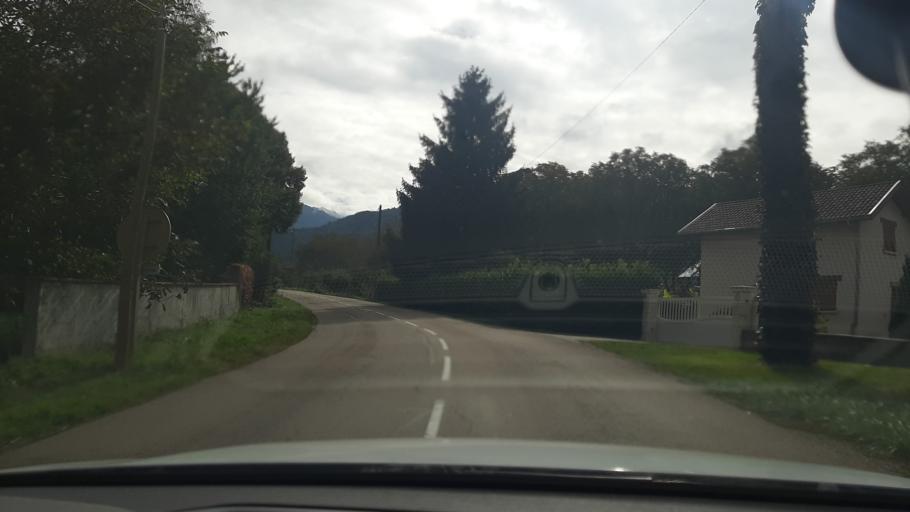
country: FR
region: Rhone-Alpes
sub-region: Departement de la Savoie
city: Montmelian
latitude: 45.4510
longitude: 6.0626
